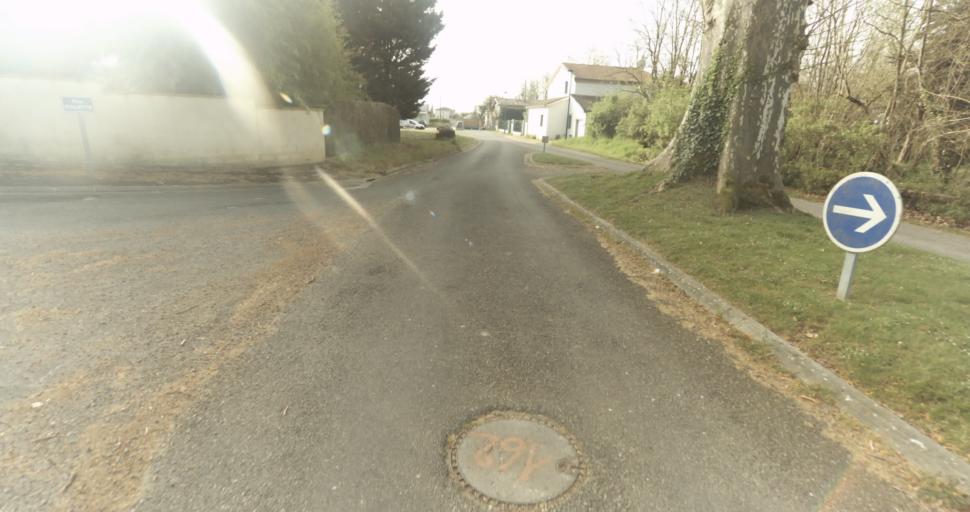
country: FR
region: Midi-Pyrenees
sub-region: Departement du Tarn-et-Garonne
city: Moissac
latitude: 44.1156
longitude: 1.1104
